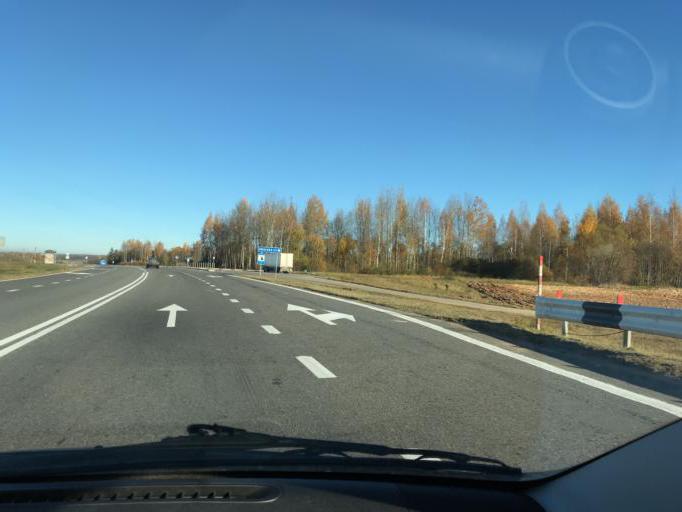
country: BY
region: Vitebsk
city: Vitebsk
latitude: 55.0869
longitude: 30.3084
